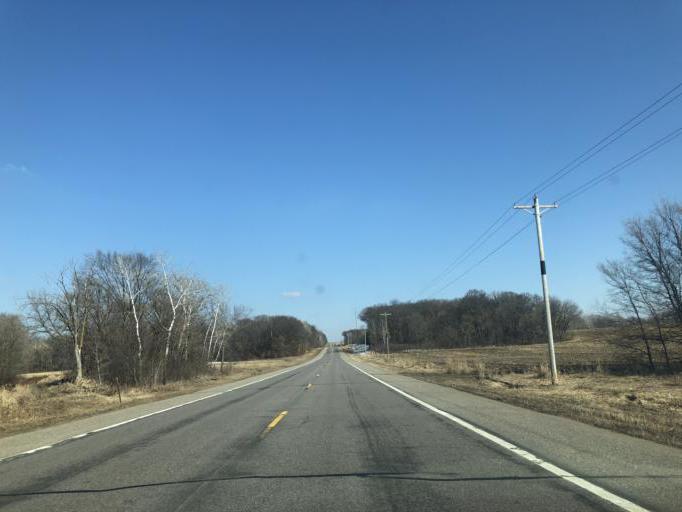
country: US
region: Minnesota
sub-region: Sherburne County
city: Becker
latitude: 45.4297
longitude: -93.8549
